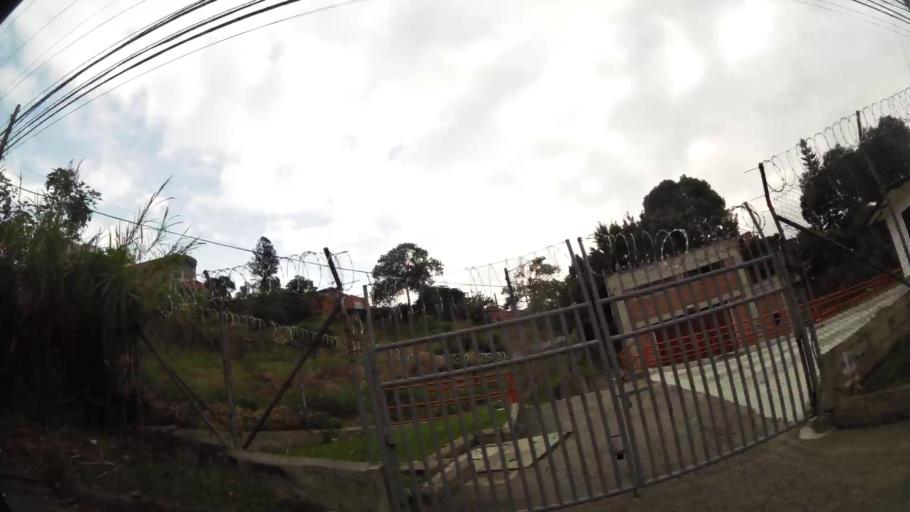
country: CO
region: Antioquia
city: Medellin
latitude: 6.2817
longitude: -75.5953
